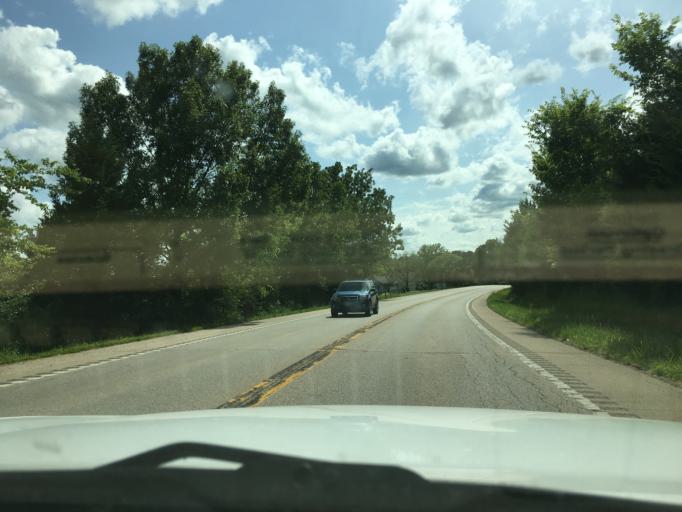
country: US
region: Missouri
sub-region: Franklin County
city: Gerald
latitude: 38.3942
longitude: -91.3566
